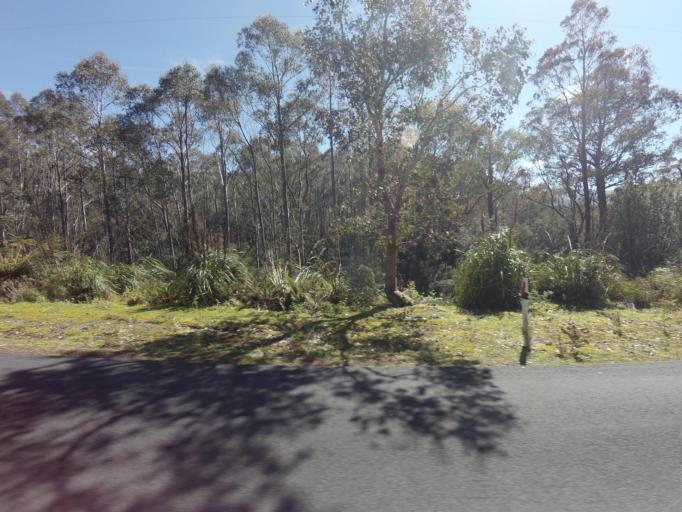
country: AU
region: Tasmania
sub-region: Derwent Valley
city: New Norfolk
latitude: -42.7276
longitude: 146.4603
